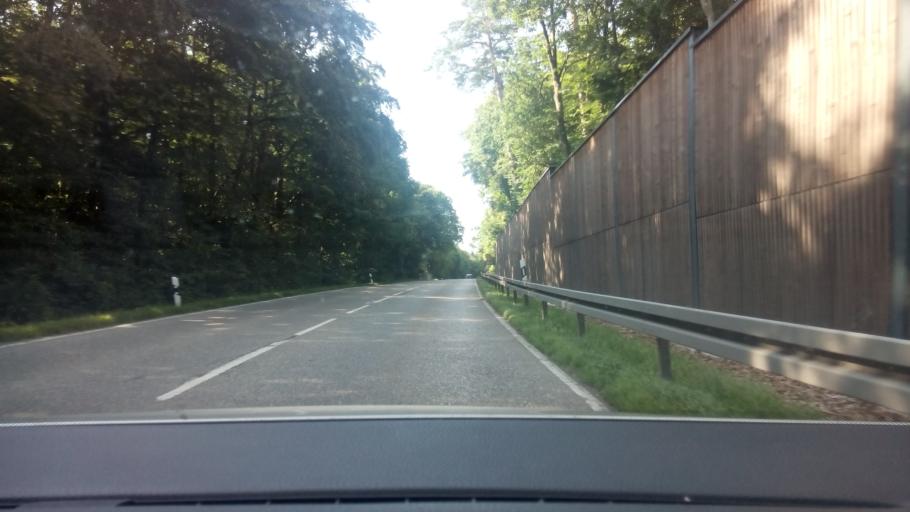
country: DE
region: Bavaria
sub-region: Upper Bavaria
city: Oberschleissheim
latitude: 48.2499
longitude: 11.5823
